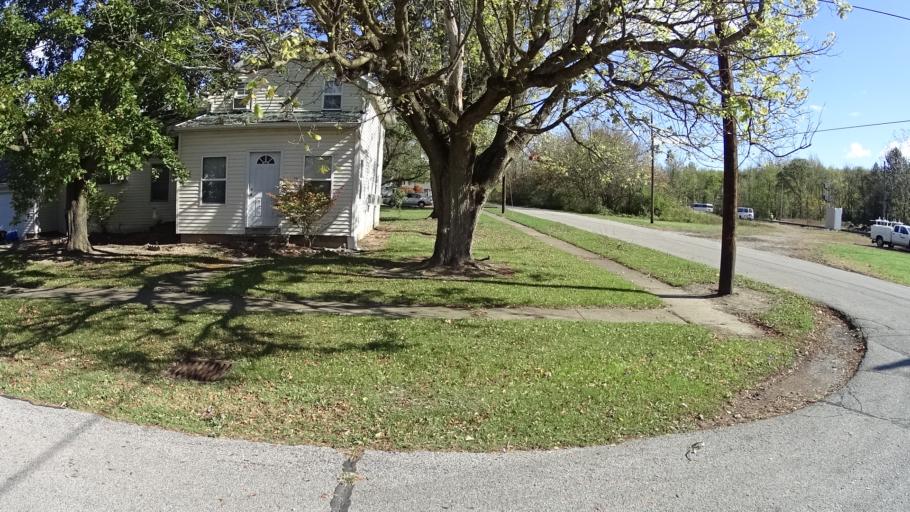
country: US
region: Ohio
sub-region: Lorain County
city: Grafton
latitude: 41.2756
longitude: -82.0572
